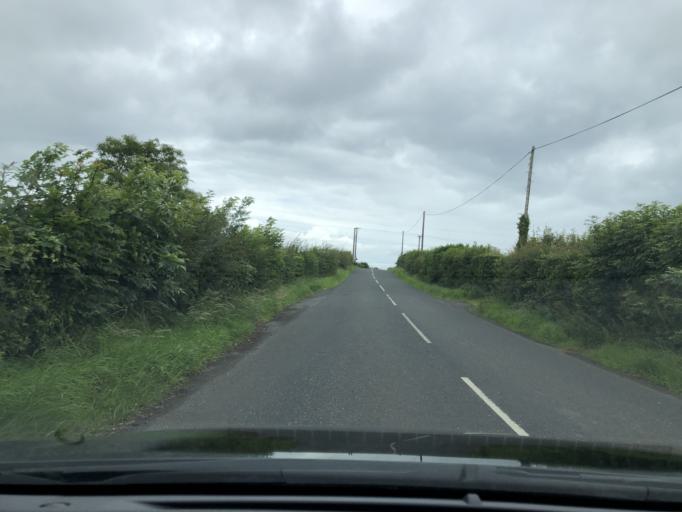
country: GB
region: Northern Ireland
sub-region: Larne District
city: Larne
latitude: 54.8453
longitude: -5.8331
